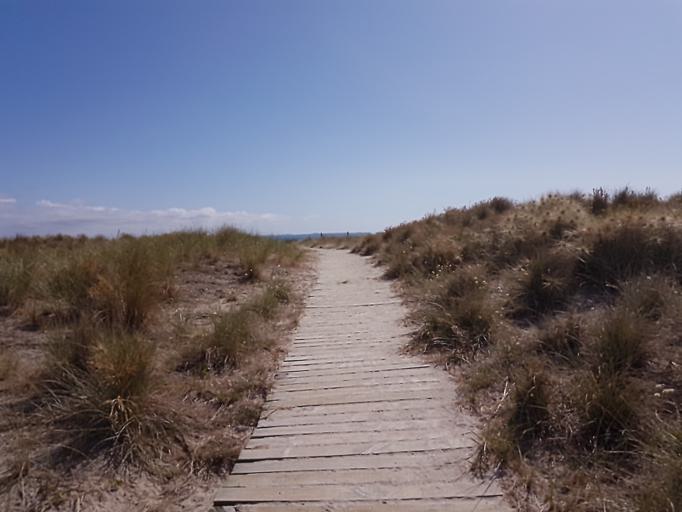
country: NZ
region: Bay of Plenty
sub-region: Tauranga City
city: Tauranga
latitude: -37.7061
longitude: 176.3138
